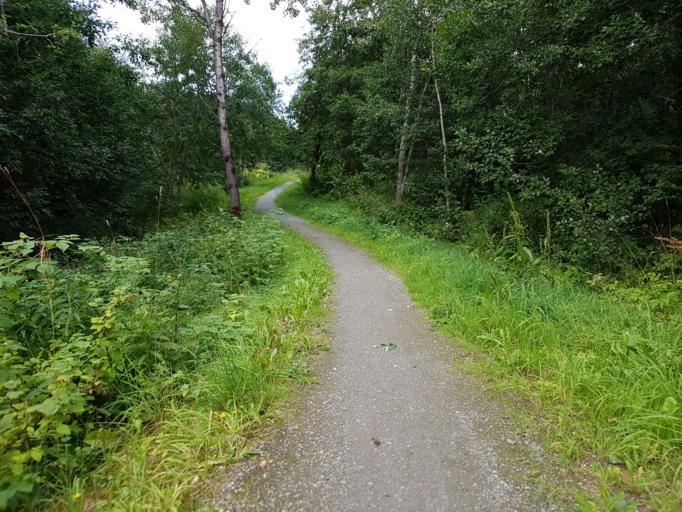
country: NO
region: Sor-Trondelag
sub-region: Trondheim
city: Trondheim
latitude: 63.4236
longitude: 10.4598
